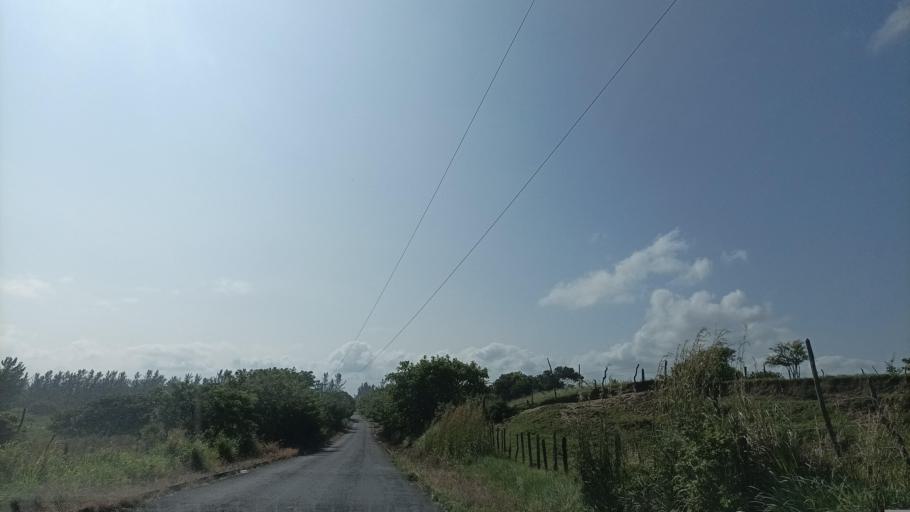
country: MX
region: Veracruz
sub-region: Pajapan
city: Pajapan
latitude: 18.2234
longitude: -94.6168
